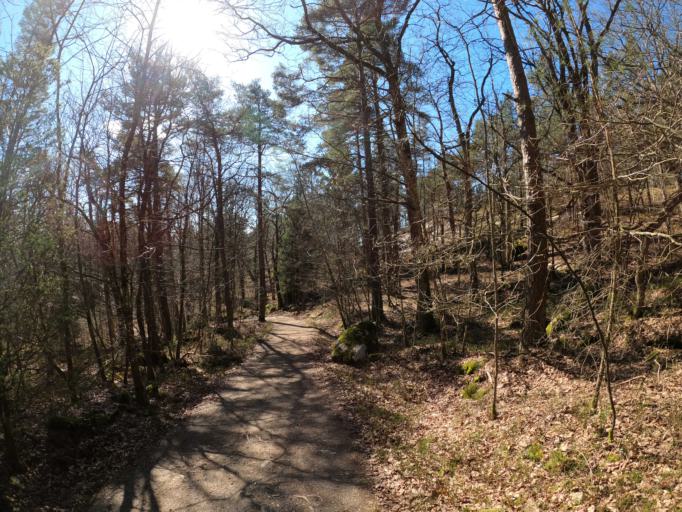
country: SE
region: Vaestra Goetaland
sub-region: Harryda Kommun
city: Molnlycke
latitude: 57.6369
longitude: 12.1279
